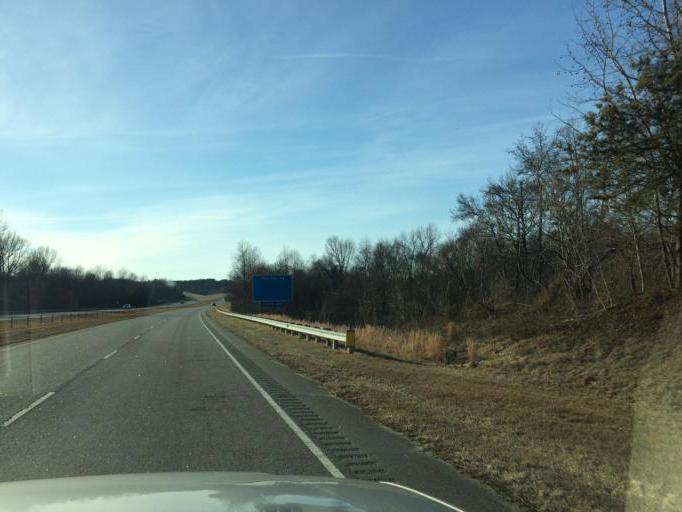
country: US
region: North Carolina
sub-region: Rutherford County
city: Forest City
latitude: 35.3070
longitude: -81.9105
